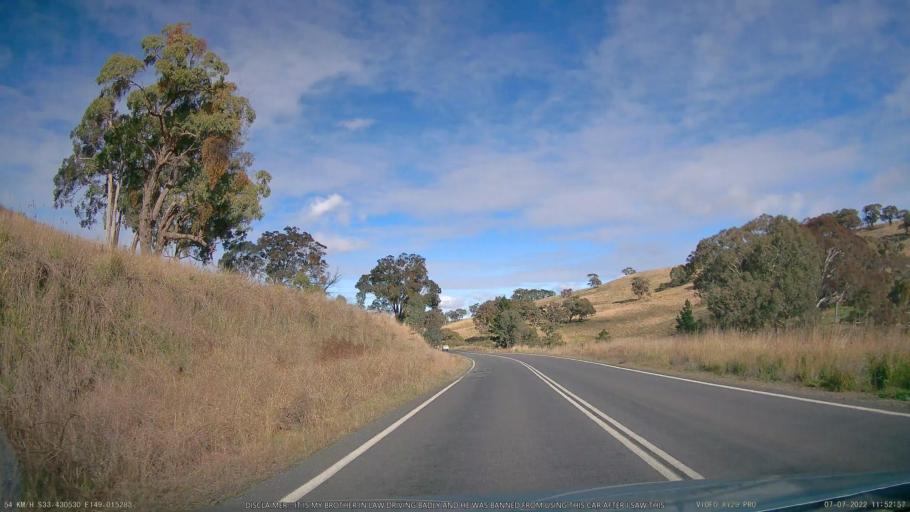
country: AU
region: New South Wales
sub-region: Orange Municipality
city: Orange
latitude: -33.4308
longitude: 149.0150
